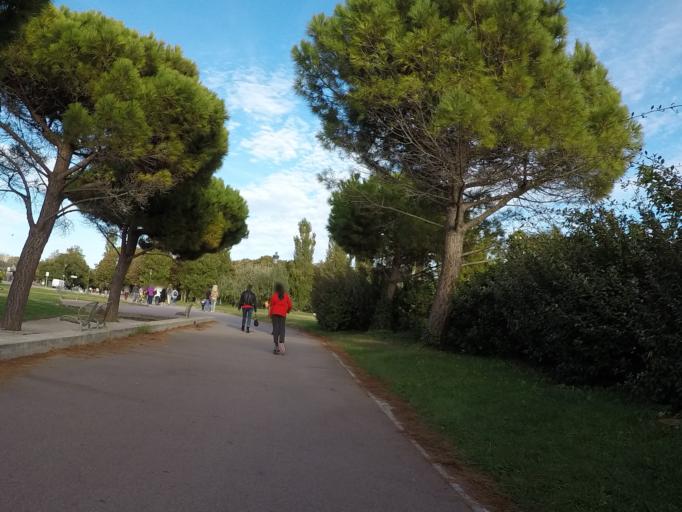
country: FR
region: Provence-Alpes-Cote d'Azur
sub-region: Departement des Bouches-du-Rhone
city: Marseille 08
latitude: 43.2608
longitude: 5.3779
